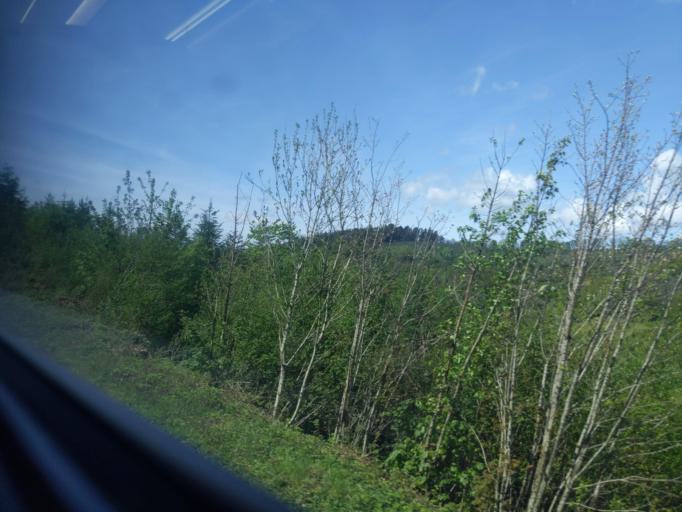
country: GB
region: England
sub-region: Cornwall
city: Lostwithiel
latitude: 50.4529
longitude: -4.5729
